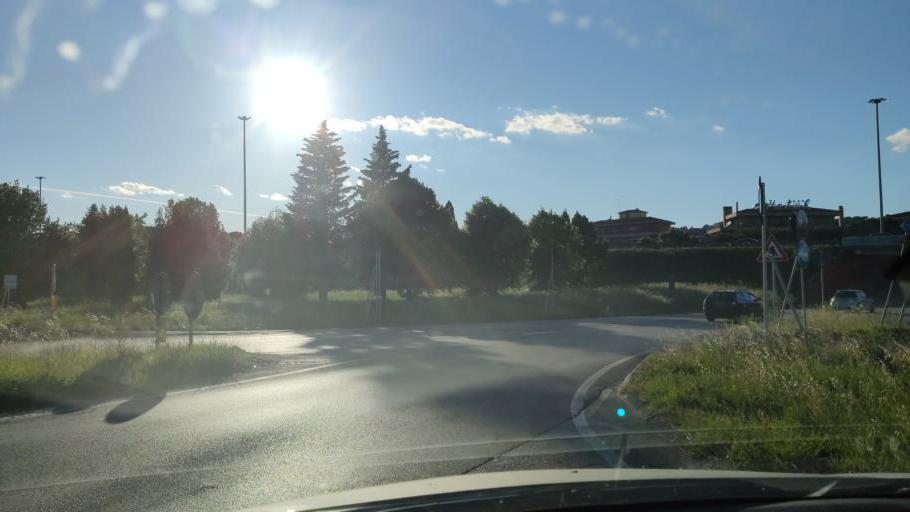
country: IT
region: Umbria
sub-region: Provincia di Perugia
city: Via Lippia
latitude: 43.0866
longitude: 12.4469
